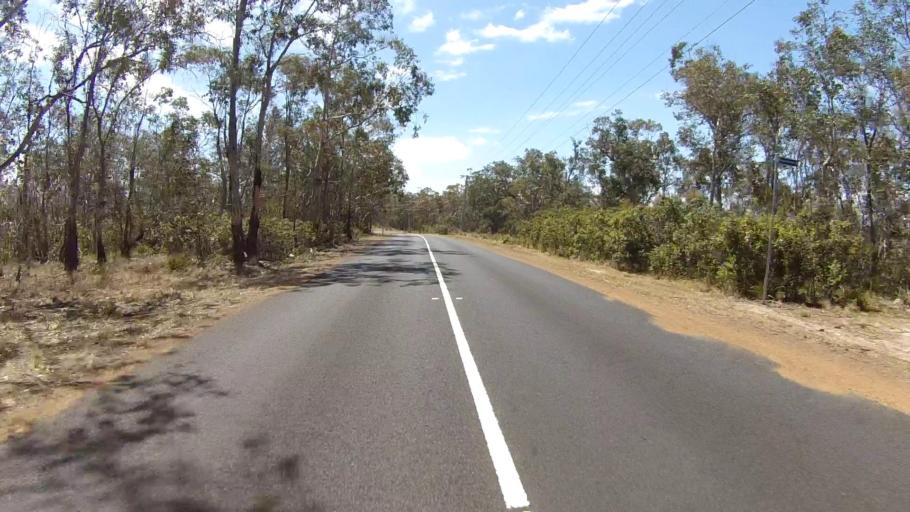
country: AU
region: Tasmania
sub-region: Clarence
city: Sandford
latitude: -43.0090
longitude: 147.4802
